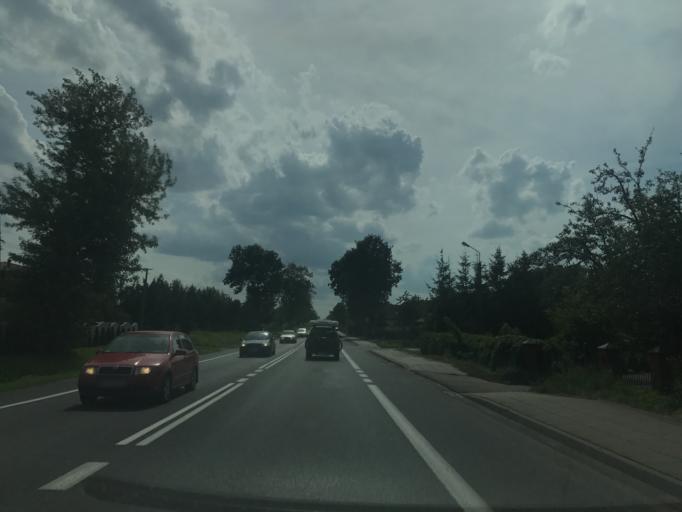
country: PL
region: Masovian Voivodeship
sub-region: Powiat mlawski
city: Mlawa
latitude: 53.0909
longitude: 20.3669
